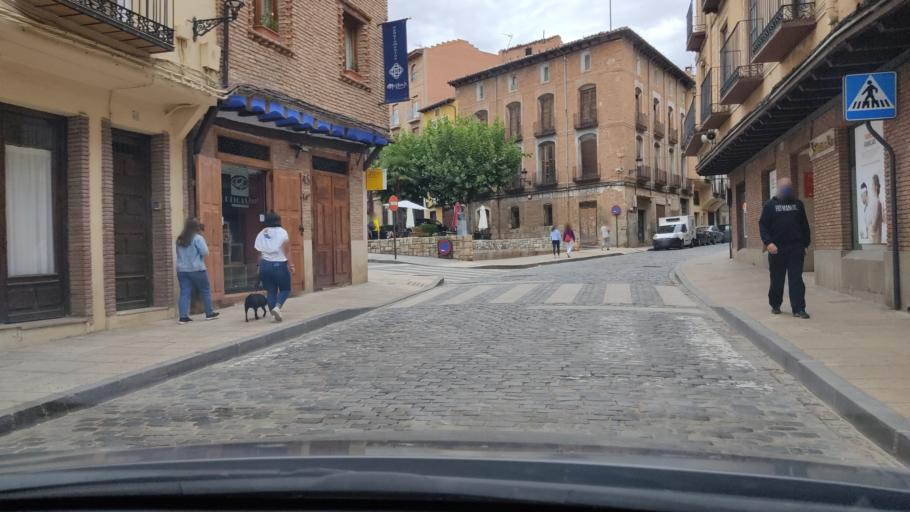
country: ES
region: Aragon
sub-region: Provincia de Zaragoza
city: Daroca
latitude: 41.1140
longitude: -1.4154
